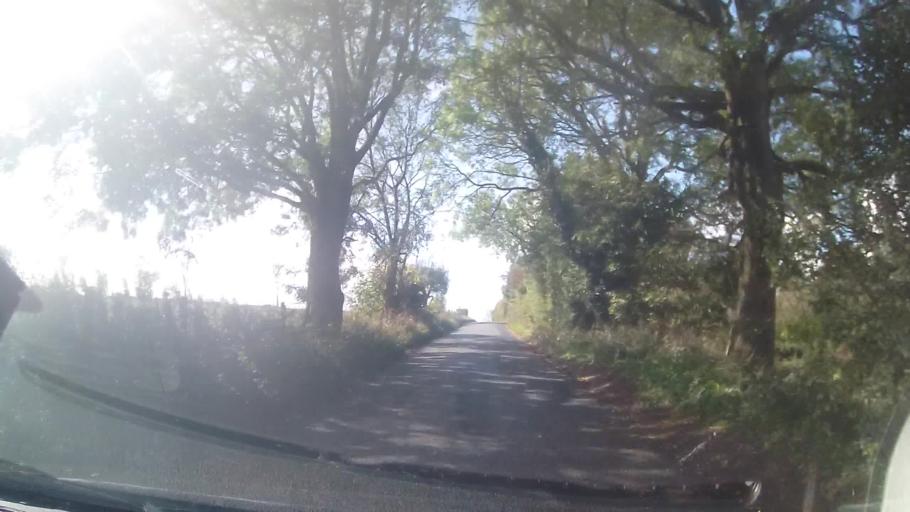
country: GB
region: England
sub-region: Worcestershire
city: Broadway
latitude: 52.0287
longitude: -1.8273
